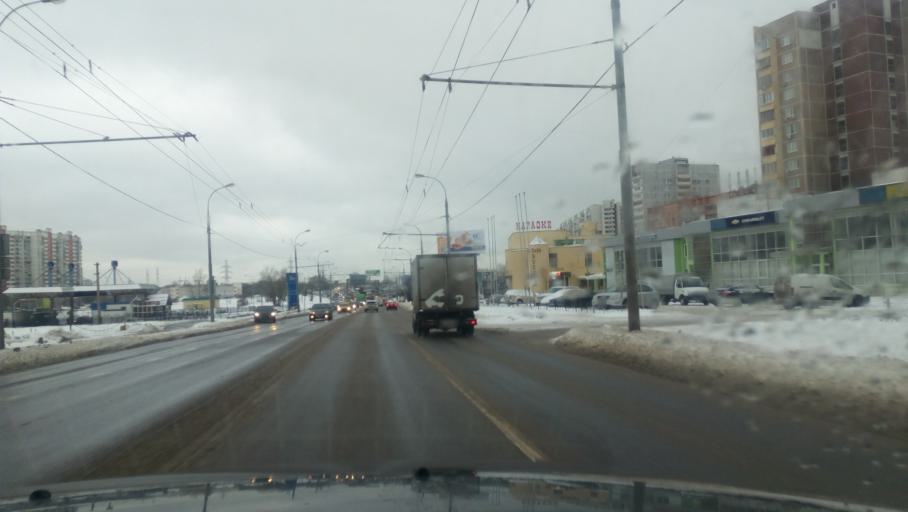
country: RU
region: Moskovskaya
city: Reutov
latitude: 55.7451
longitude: 37.8586
